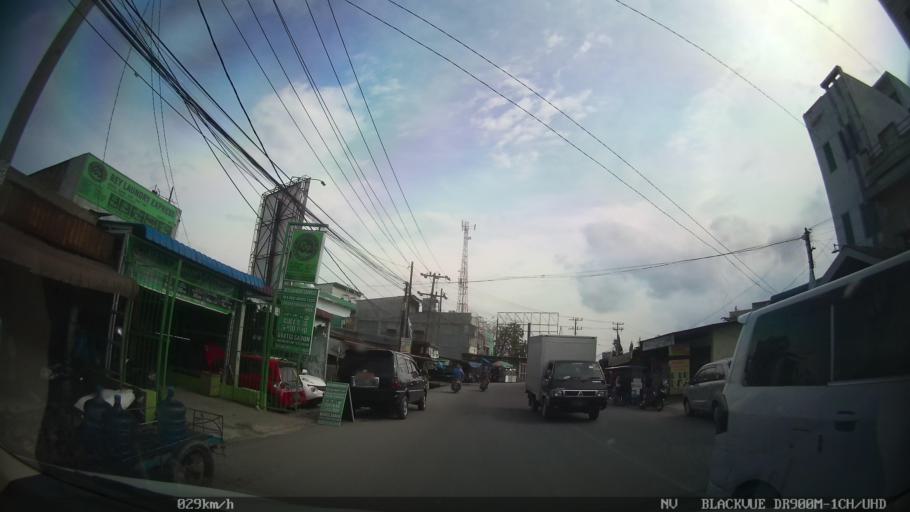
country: ID
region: North Sumatra
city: Medan
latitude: 3.6017
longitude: 98.7578
